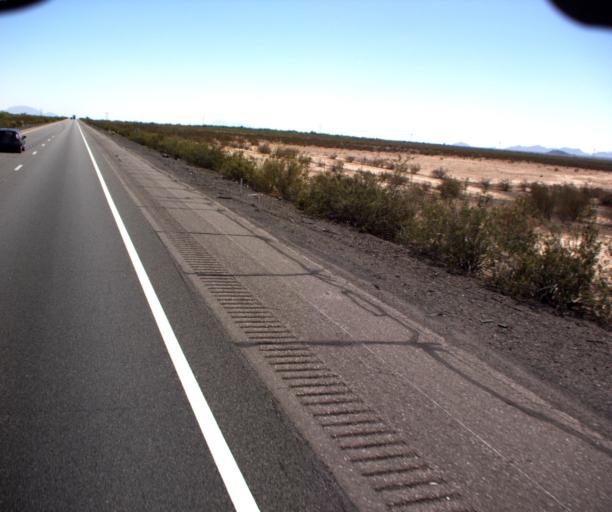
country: US
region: Arizona
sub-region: La Paz County
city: Salome
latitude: 33.5808
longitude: -113.4330
